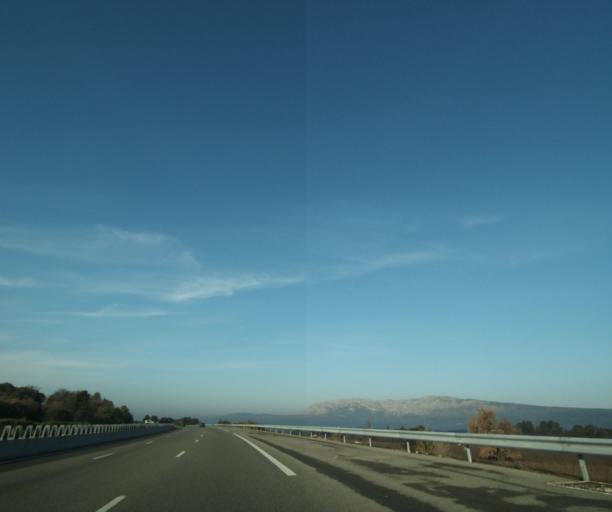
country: FR
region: Provence-Alpes-Cote d'Azur
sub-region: Departement du Var
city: Pourrieres
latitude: 43.4816
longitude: 5.7396
